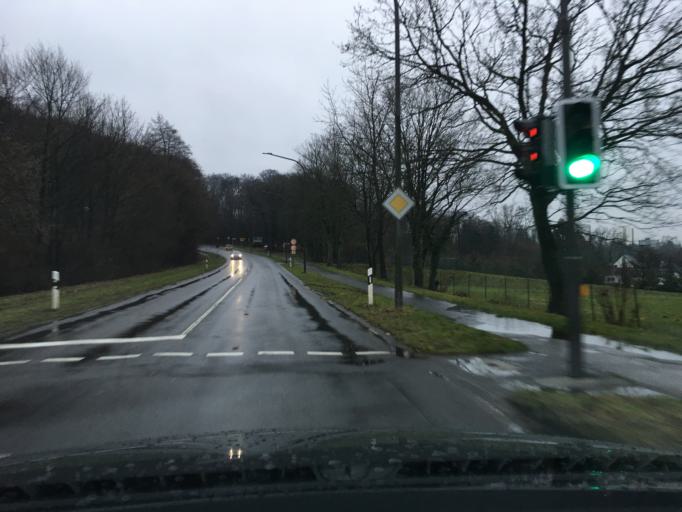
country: DE
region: North Rhine-Westphalia
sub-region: Regierungsbezirk Dusseldorf
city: Wuppertal
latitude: 51.2867
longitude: 7.1104
